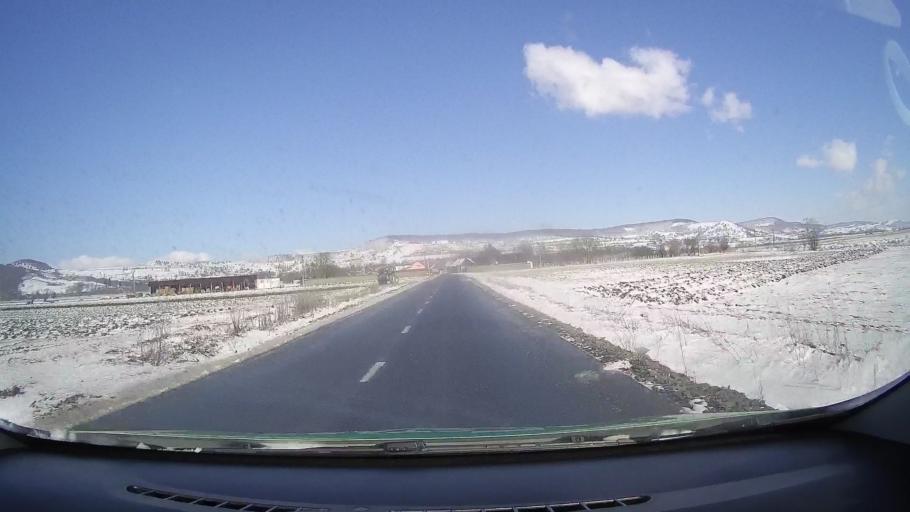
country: RO
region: Sibiu
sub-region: Comuna Avrig
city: Avrig
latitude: 45.7526
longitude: 24.3917
